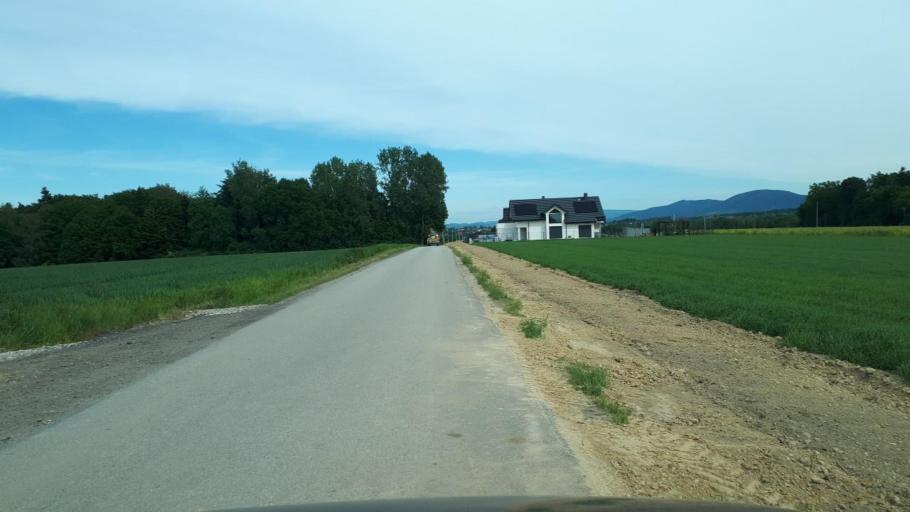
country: PL
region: Silesian Voivodeship
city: Janowice
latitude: 49.8871
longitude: 19.1181
